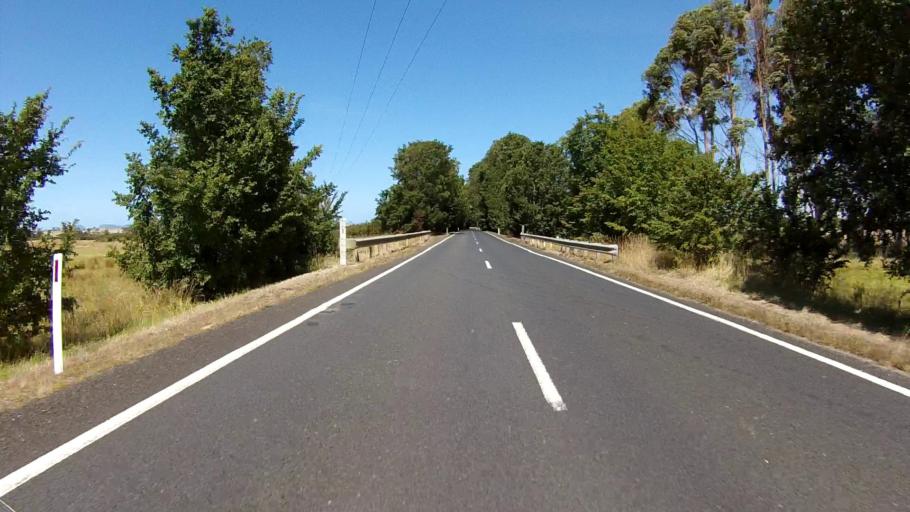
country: AU
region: Tasmania
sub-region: Break O'Day
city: St Helens
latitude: -42.0607
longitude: 148.0616
